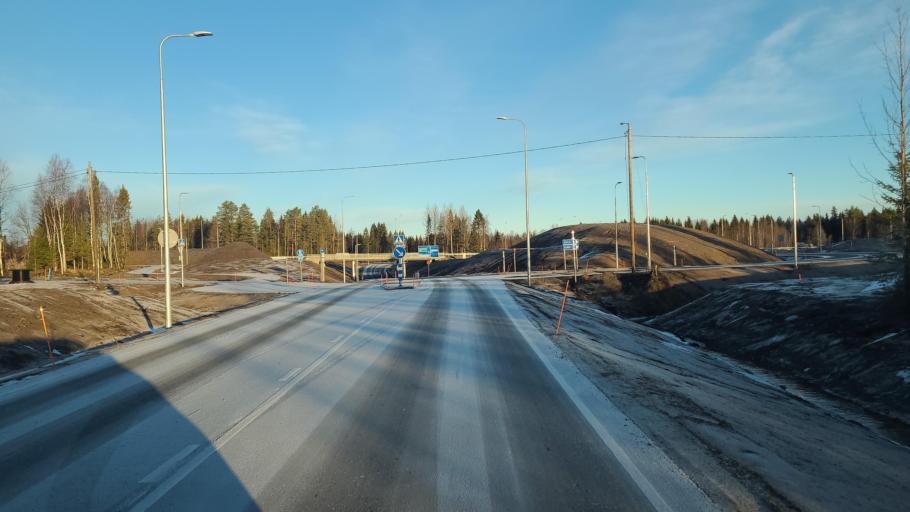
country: FI
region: Lapland
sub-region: Kemi-Tornio
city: Kemi
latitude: 65.6769
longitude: 24.7438
